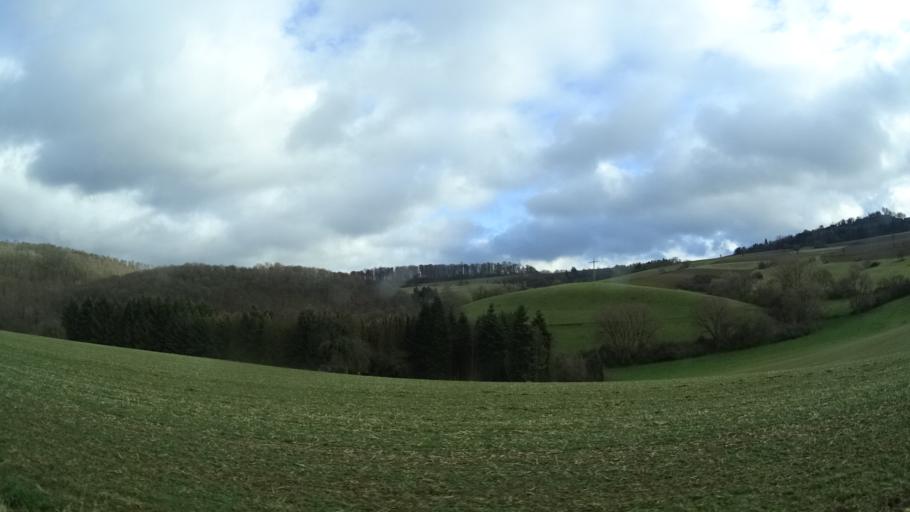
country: DE
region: Rheinland-Pfalz
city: Wurzweiler
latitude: 49.6505
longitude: 7.8668
